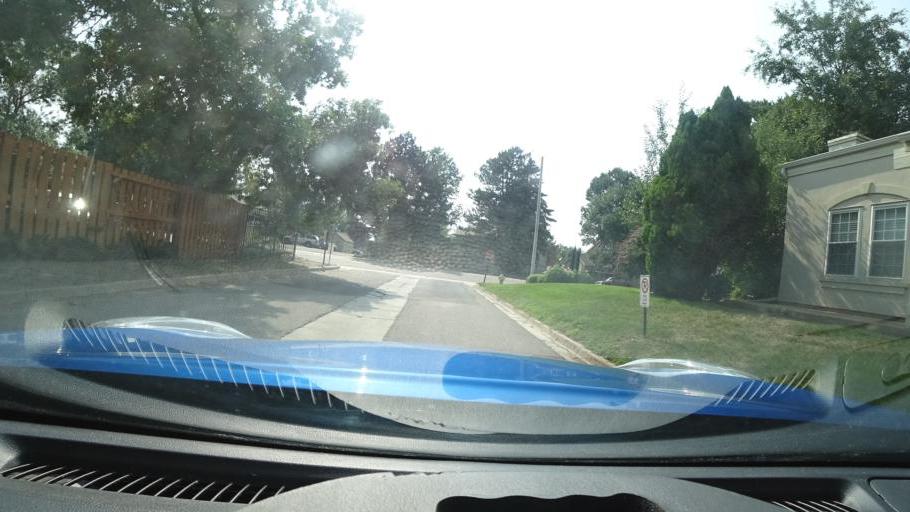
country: US
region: Colorado
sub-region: Adams County
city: Aurora
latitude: 39.6629
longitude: -104.8388
